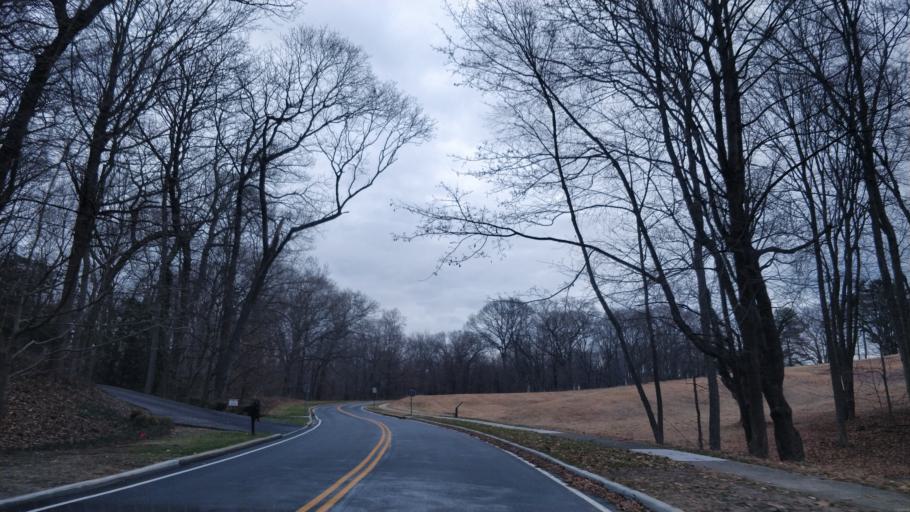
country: US
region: New York
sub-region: Nassau County
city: Oyster Bay Cove
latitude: 40.8845
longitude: -73.5030
